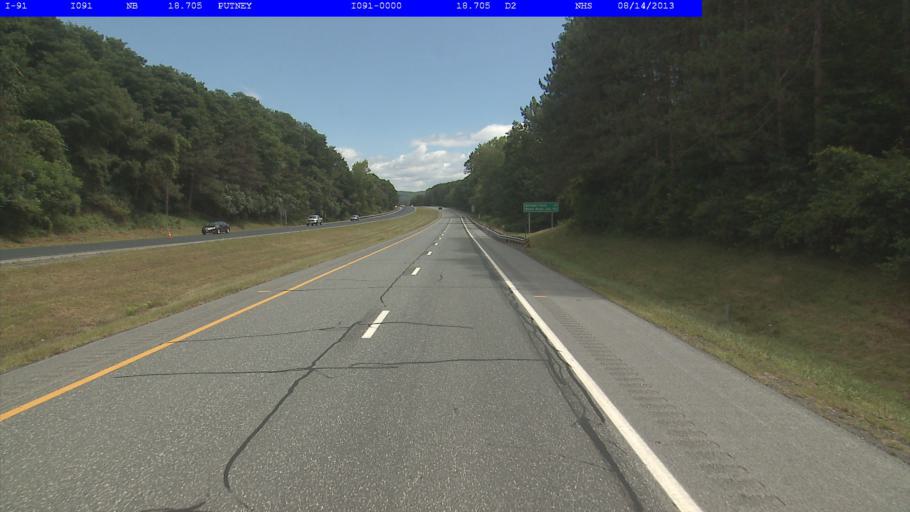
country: US
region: New Hampshire
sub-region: Cheshire County
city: Westmoreland
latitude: 42.9660
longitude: -72.5102
